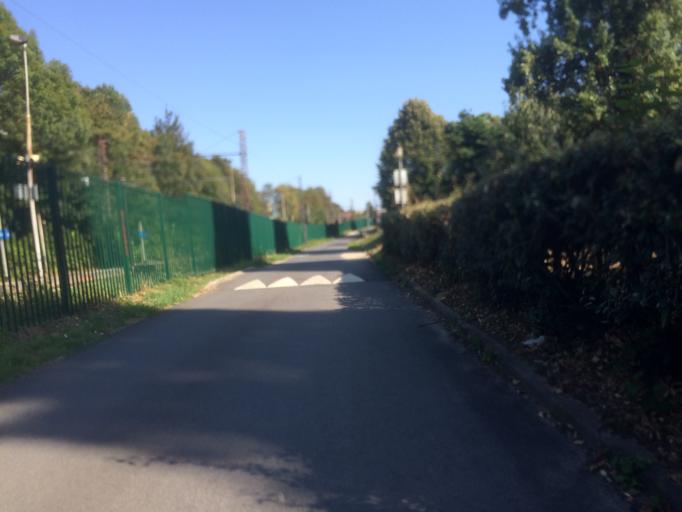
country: FR
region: Ile-de-France
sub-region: Departement de l'Essonne
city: Villemoisson-sur-Orge
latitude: 48.6769
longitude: 2.3314
